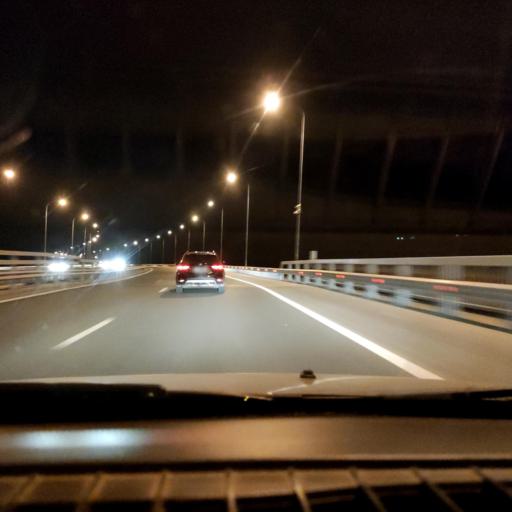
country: RU
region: Samara
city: Bereza
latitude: 53.5006
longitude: 50.1166
